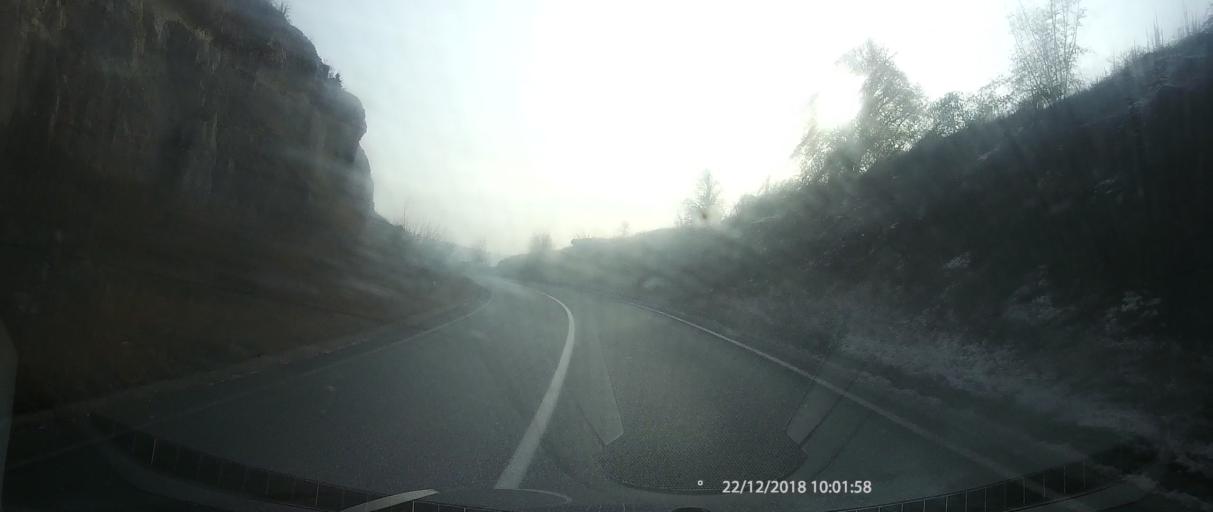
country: MK
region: Opstina Rankovce
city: Rankovce
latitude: 42.1467
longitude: 22.0026
